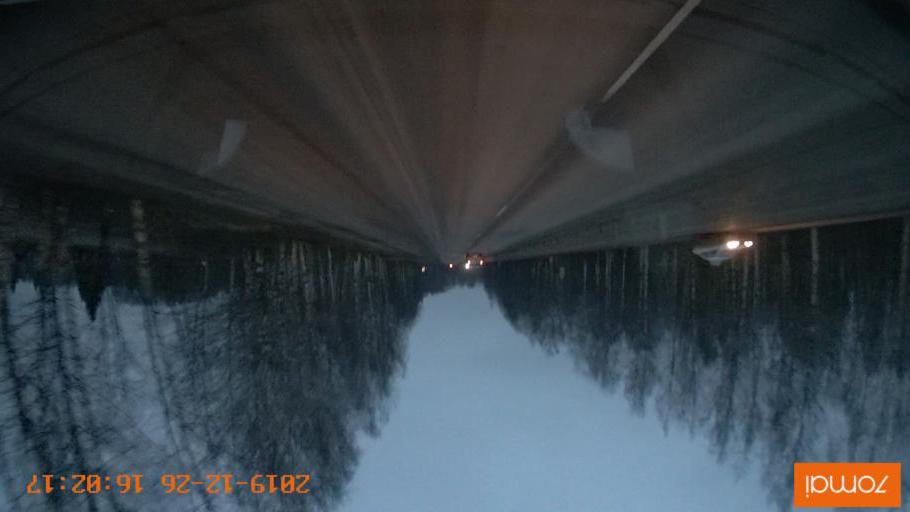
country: RU
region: Jaroslavl
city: Rybinsk
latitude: 58.0129
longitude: 38.8315
